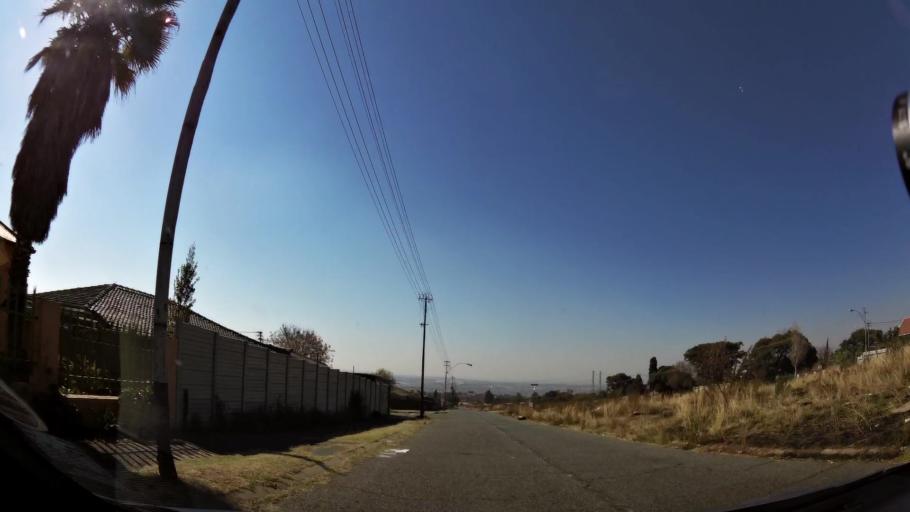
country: ZA
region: Gauteng
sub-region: City of Johannesburg Metropolitan Municipality
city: Johannesburg
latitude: -26.2560
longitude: 28.0893
